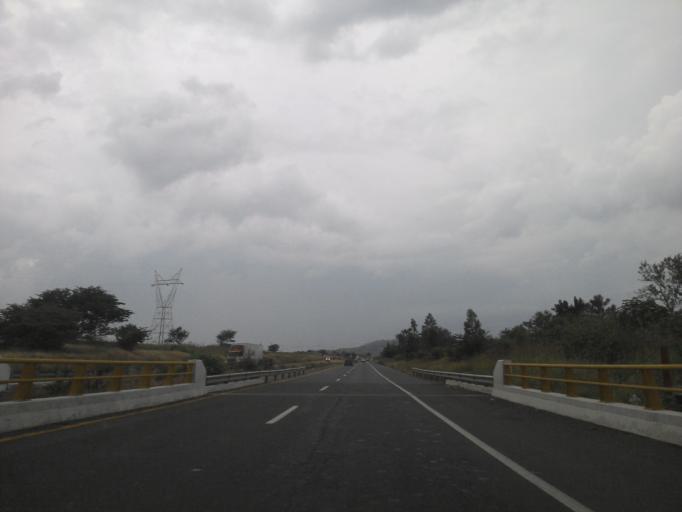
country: MX
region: Jalisco
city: Puente Grande
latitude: 20.5747
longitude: -103.1411
